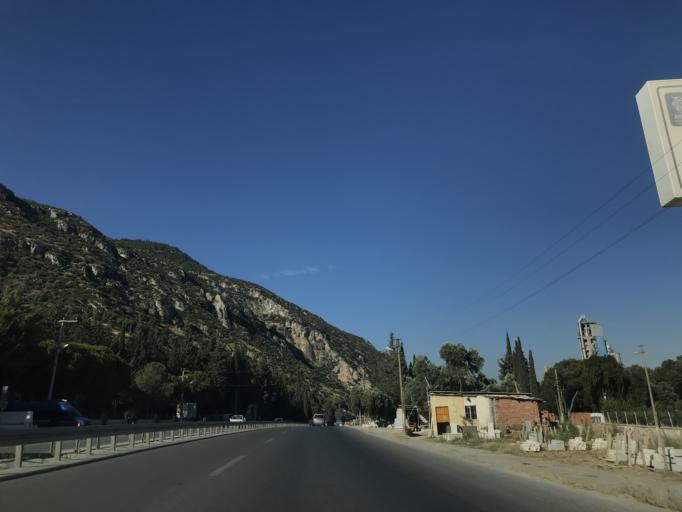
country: TR
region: Aydin
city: Soeke
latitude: 37.7701
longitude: 27.4279
